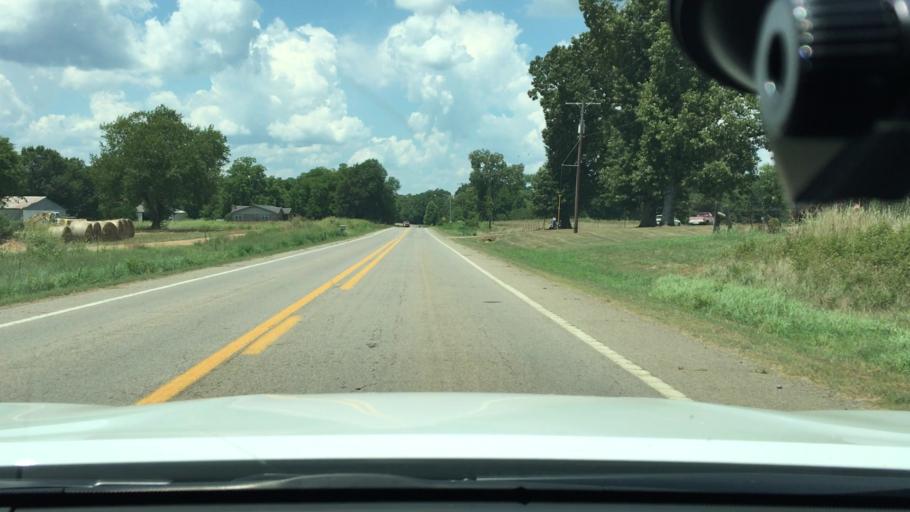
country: US
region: Arkansas
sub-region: Logan County
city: Booneville
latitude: 35.1509
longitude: -93.8250
